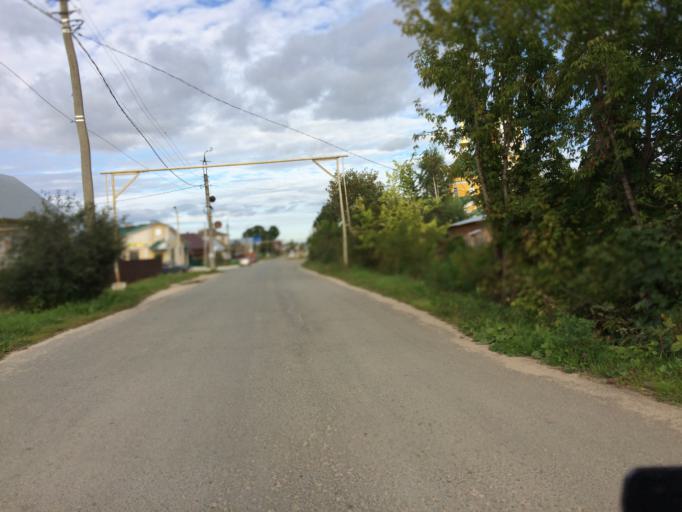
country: RU
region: Mariy-El
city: Yoshkar-Ola
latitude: 56.6505
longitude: 47.9789
